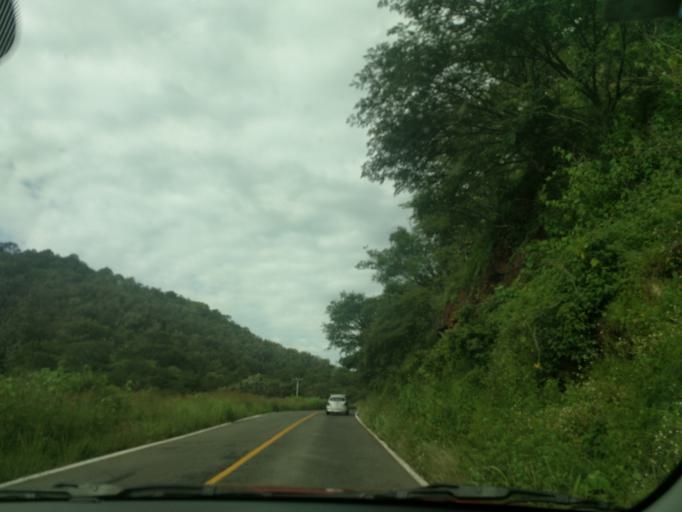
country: MX
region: Jalisco
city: Ameca
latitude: 20.5435
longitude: -104.2807
